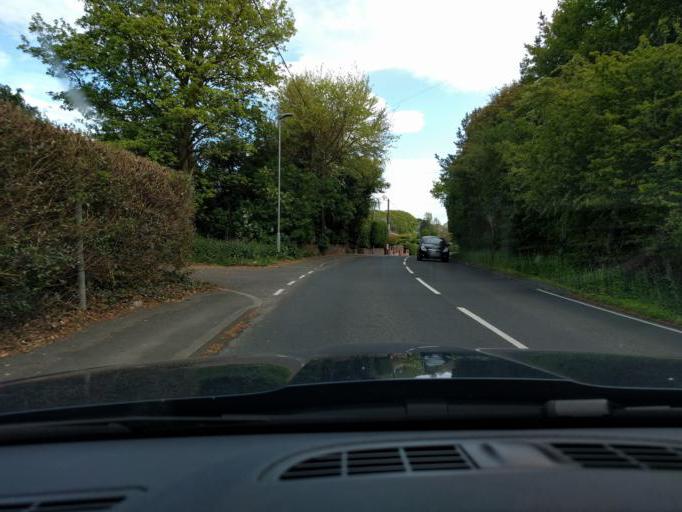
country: GB
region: England
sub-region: Northumberland
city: Bedlington
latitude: 55.1168
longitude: -1.6253
